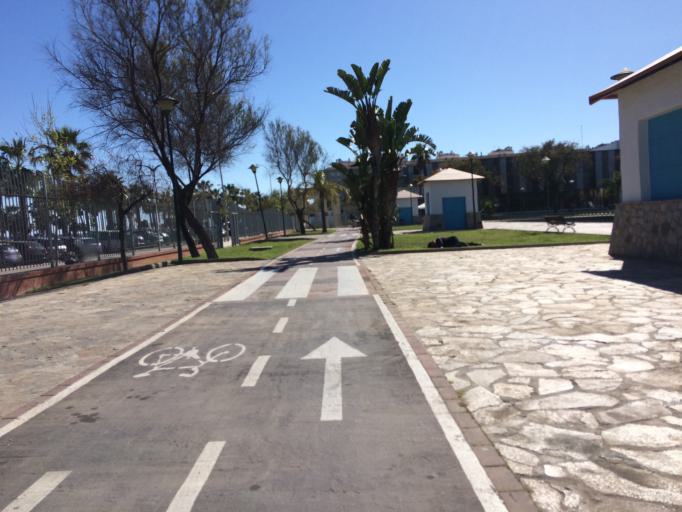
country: ES
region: Andalusia
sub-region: Provincia de Malaga
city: Malaga
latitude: 36.7055
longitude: -4.4317
